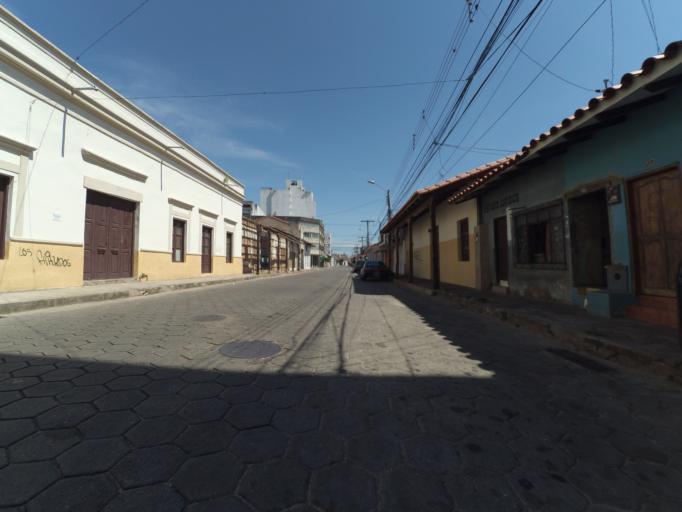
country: BO
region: Santa Cruz
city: Santa Cruz de la Sierra
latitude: -17.7889
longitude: -63.1831
